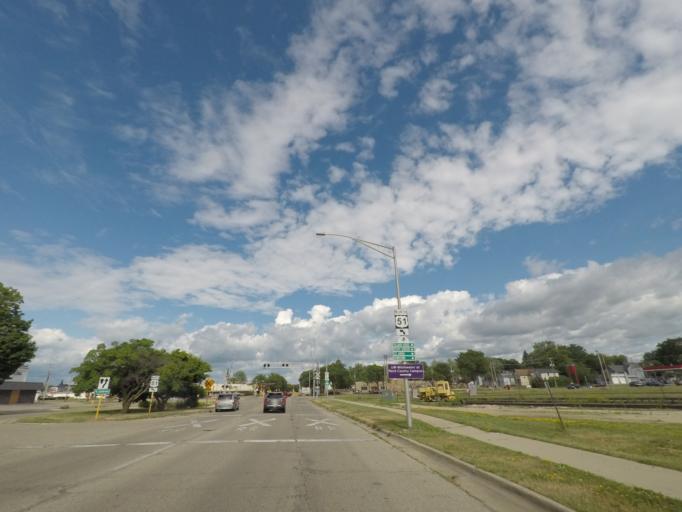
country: US
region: Wisconsin
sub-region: Rock County
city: Janesville
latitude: 42.6793
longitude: -89.0335
